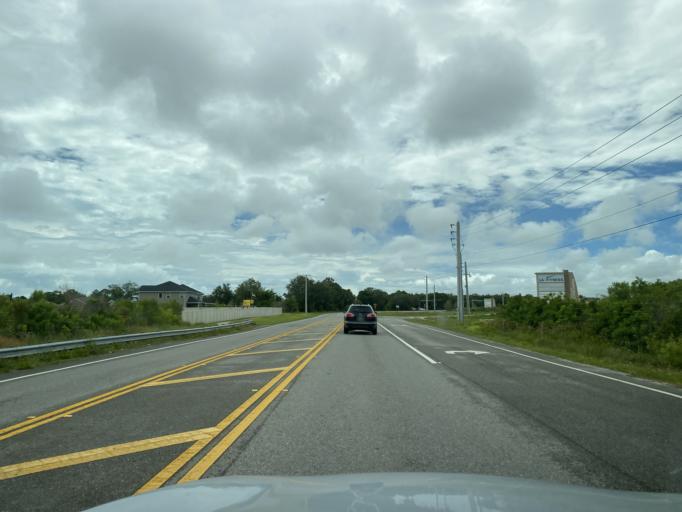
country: US
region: Florida
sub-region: Brevard County
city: West Melbourne
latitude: 28.0394
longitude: -80.6525
